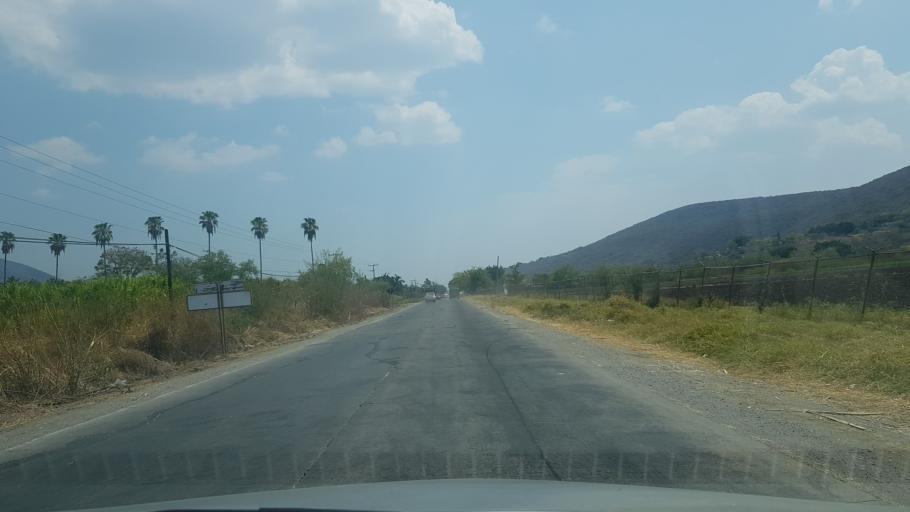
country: MX
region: Morelos
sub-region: Tlaltizapan de Zapata
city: Colonia Palo Prieto (Chipitongo)
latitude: 18.7285
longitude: -99.1240
